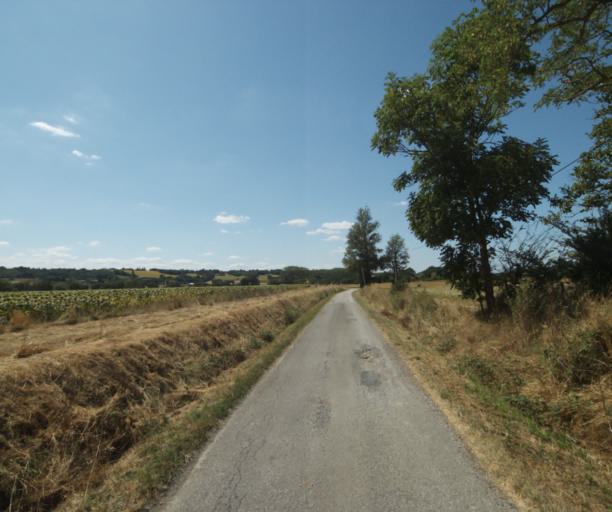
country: FR
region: Midi-Pyrenees
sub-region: Departement de la Haute-Garonne
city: Saint-Felix-Lauragais
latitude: 43.4843
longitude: 1.8856
